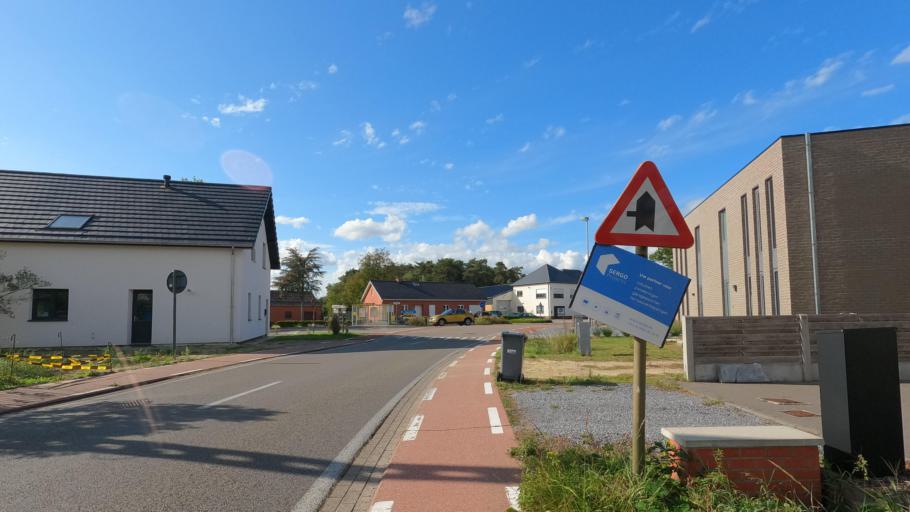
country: BE
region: Flanders
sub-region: Provincie Antwerpen
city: Herselt
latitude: 51.0297
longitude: 4.8966
